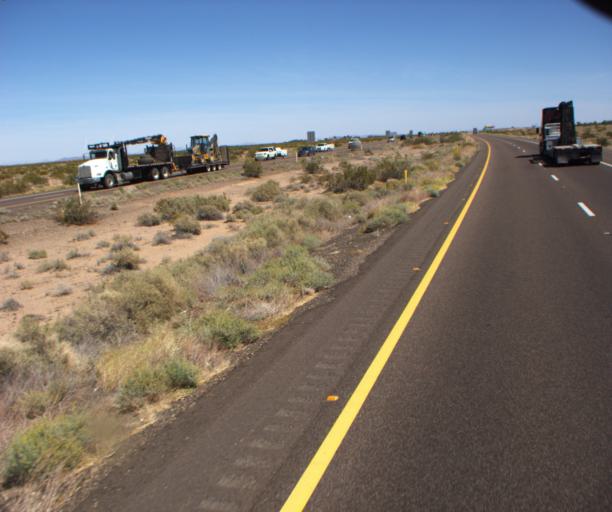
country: US
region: Arizona
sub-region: Yuma County
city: Wellton
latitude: 32.7906
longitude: -113.5576
